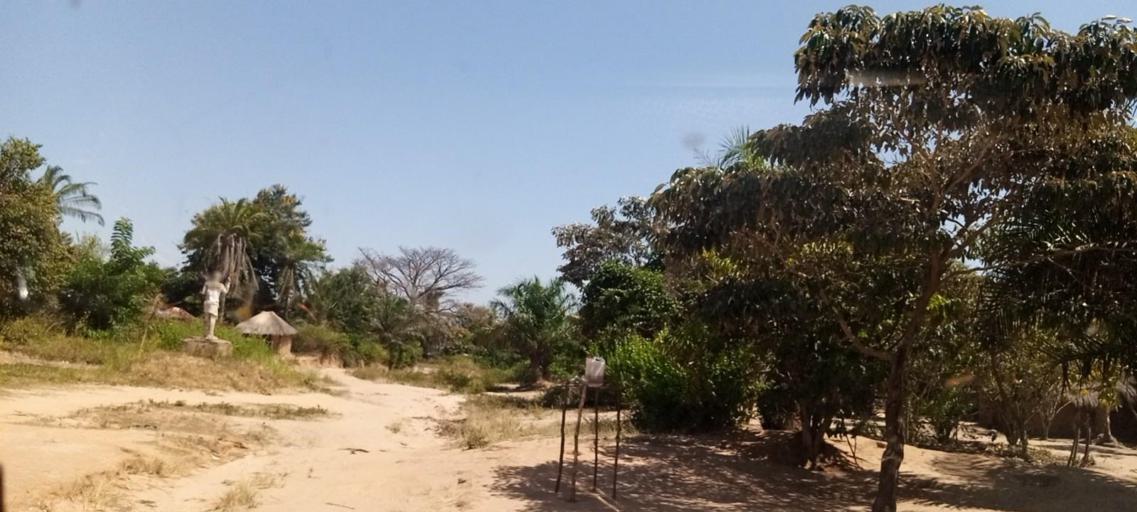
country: CD
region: Kasai-Oriental
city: Kabinda
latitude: -5.9553
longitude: 24.8021
